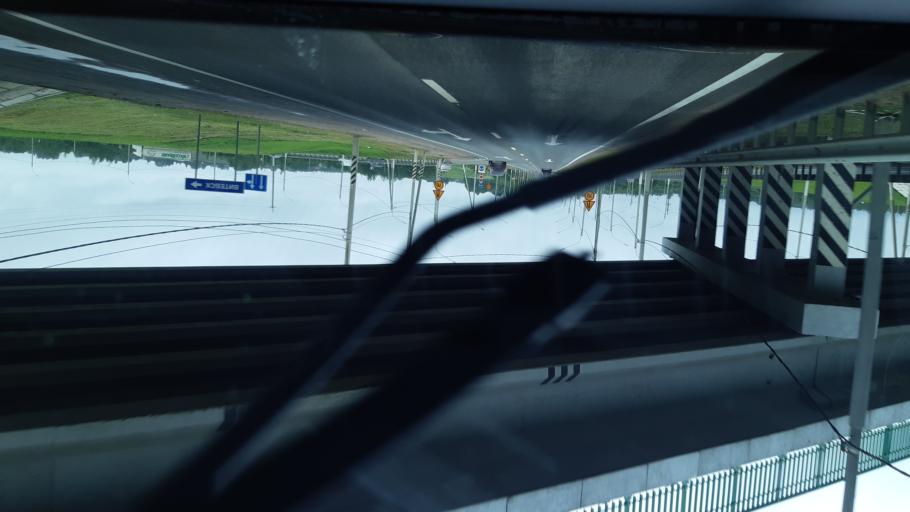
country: RU
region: Smolensk
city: Talashkino
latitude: 54.7050
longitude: 32.1186
